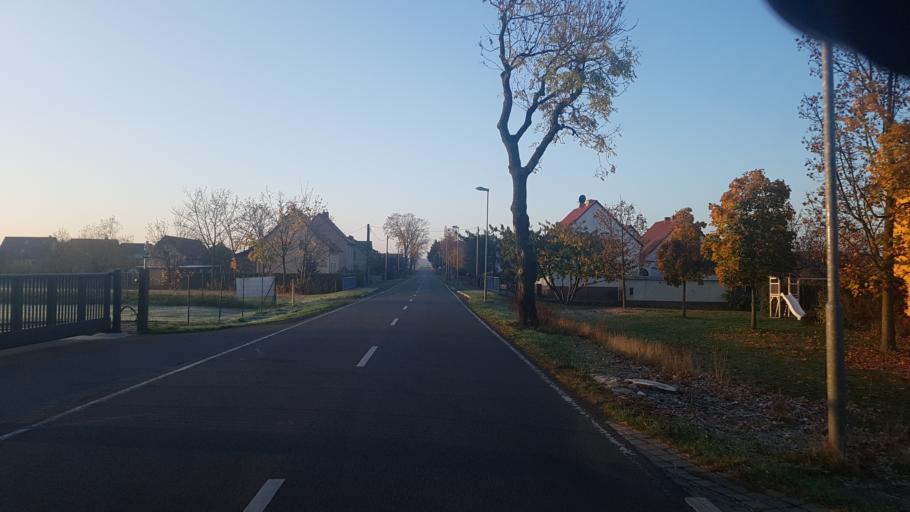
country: DE
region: Saxony
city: Torgau
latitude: 51.4971
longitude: 12.9918
